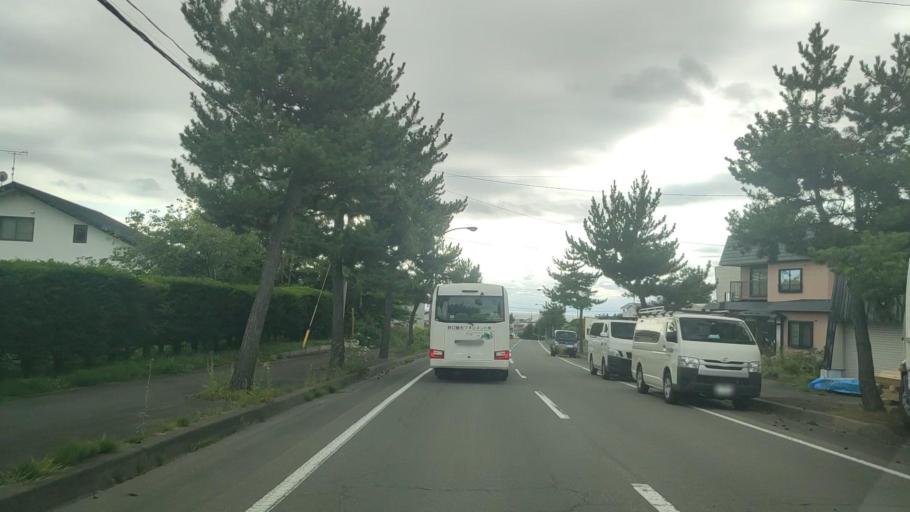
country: JP
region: Hokkaido
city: Date
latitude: 42.5486
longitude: 140.7707
